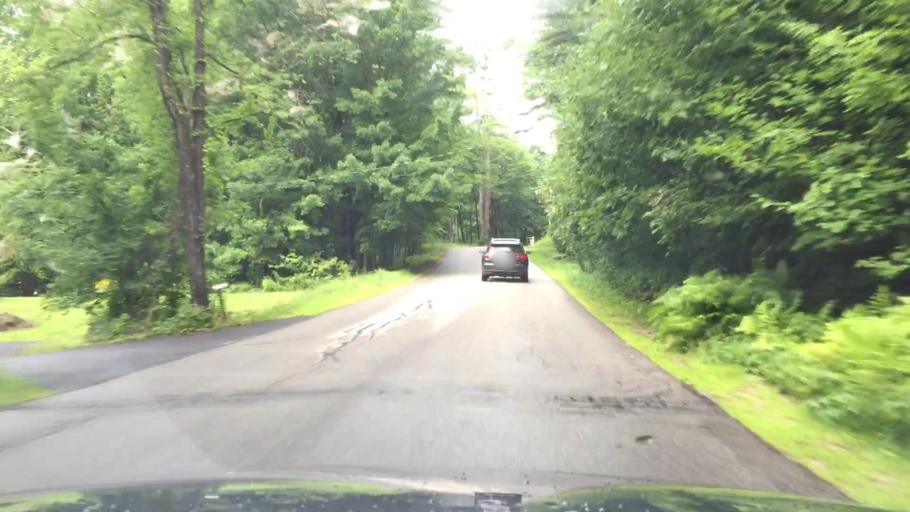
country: US
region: New Hampshire
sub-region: Grafton County
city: Holderness
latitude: 43.7261
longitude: -71.5722
